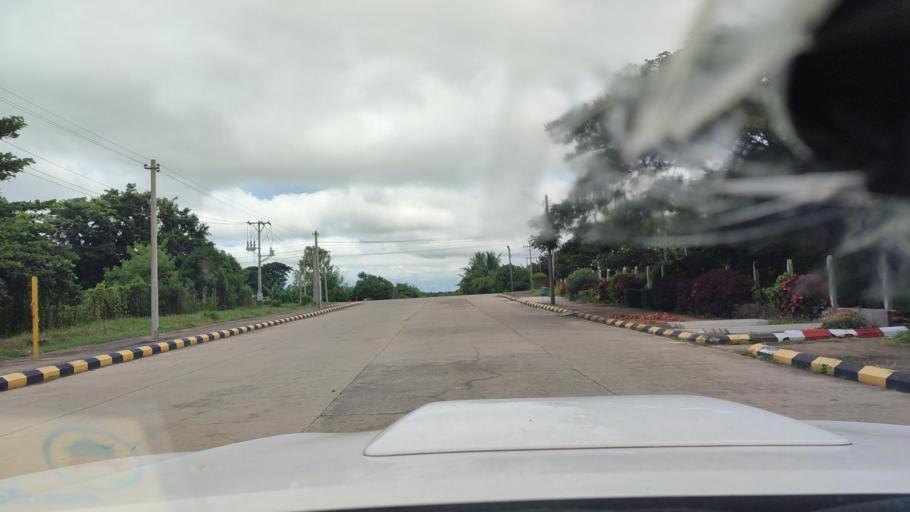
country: MM
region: Mandalay
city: Nay Pyi Taw
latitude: 19.7385
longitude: 96.0609
